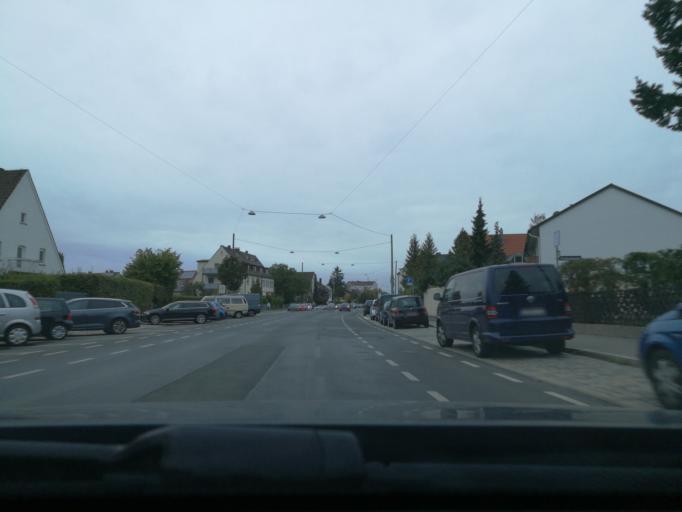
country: DE
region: Bavaria
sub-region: Regierungsbezirk Mittelfranken
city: Furth
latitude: 49.4771
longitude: 11.0055
